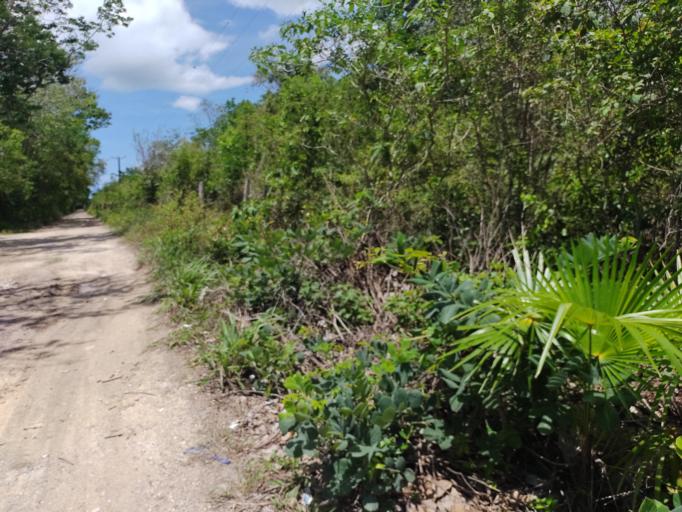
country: MX
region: Quintana Roo
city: San Miguel de Cozumel
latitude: 20.4978
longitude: -86.9025
